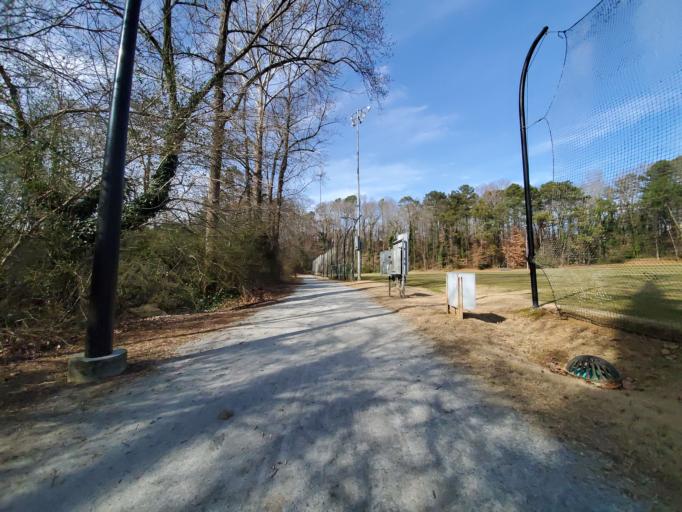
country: US
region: Georgia
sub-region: DeKalb County
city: Druid Hills
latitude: 33.8006
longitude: -84.3339
